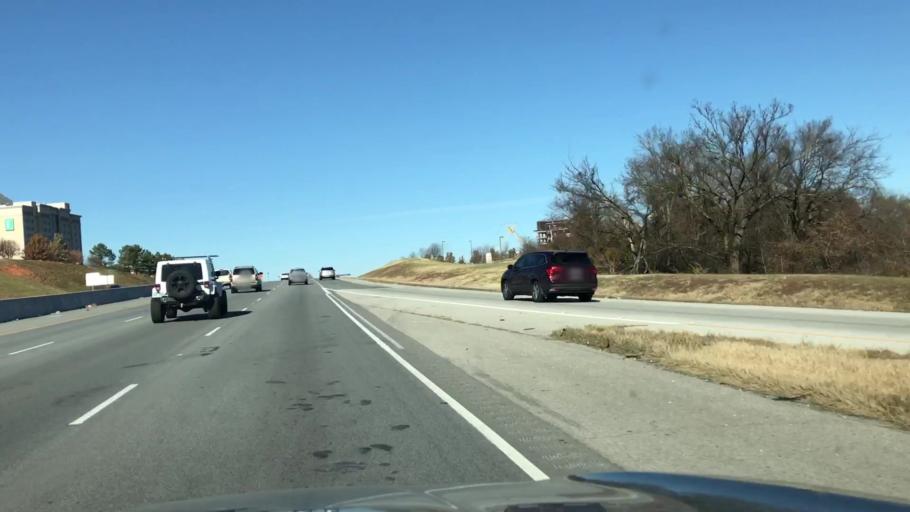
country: US
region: Arkansas
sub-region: Benton County
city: Cave Springs
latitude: 36.3035
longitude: -94.1820
